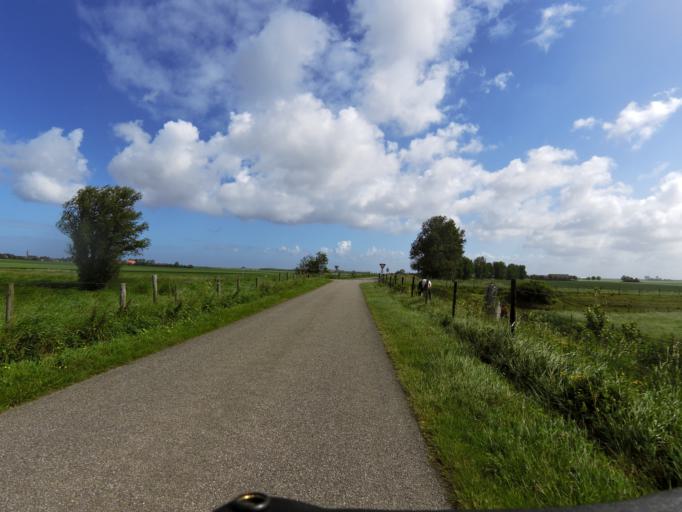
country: NL
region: South Holland
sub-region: Gemeente Goeree-Overflakkee
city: Ouddorp
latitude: 51.7015
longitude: 3.9593
